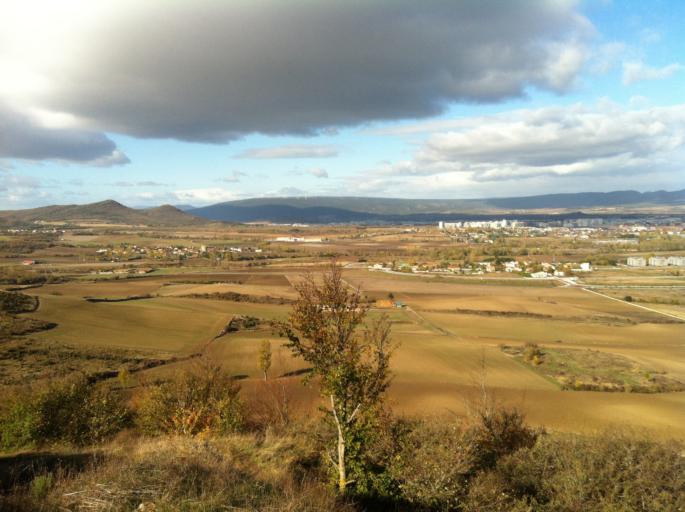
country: ES
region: Basque Country
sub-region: Provincia de Alava
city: Gasteiz / Vitoria
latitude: 42.8169
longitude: -2.6628
